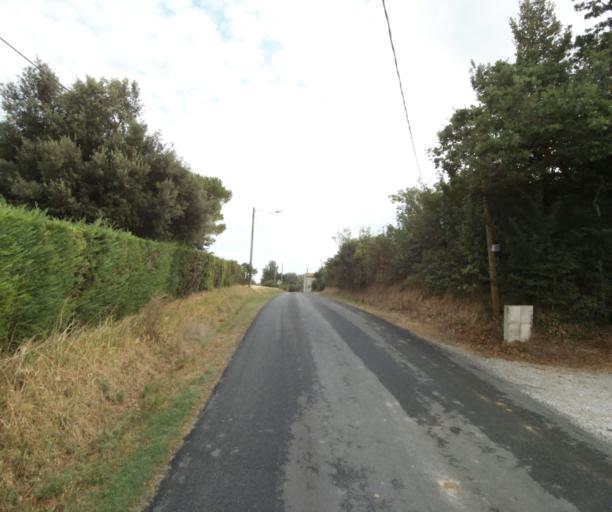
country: FR
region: Midi-Pyrenees
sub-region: Departement de la Haute-Garonne
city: Revel
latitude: 43.4507
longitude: 1.9690
